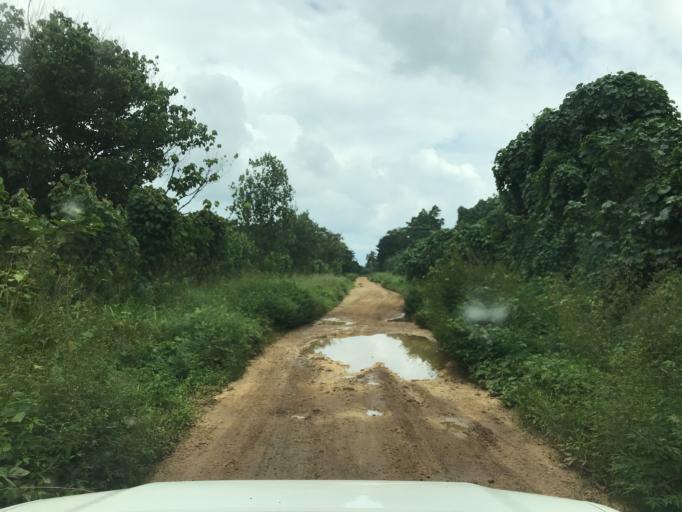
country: VU
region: Sanma
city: Port-Olry
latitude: -15.1865
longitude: 167.0092
